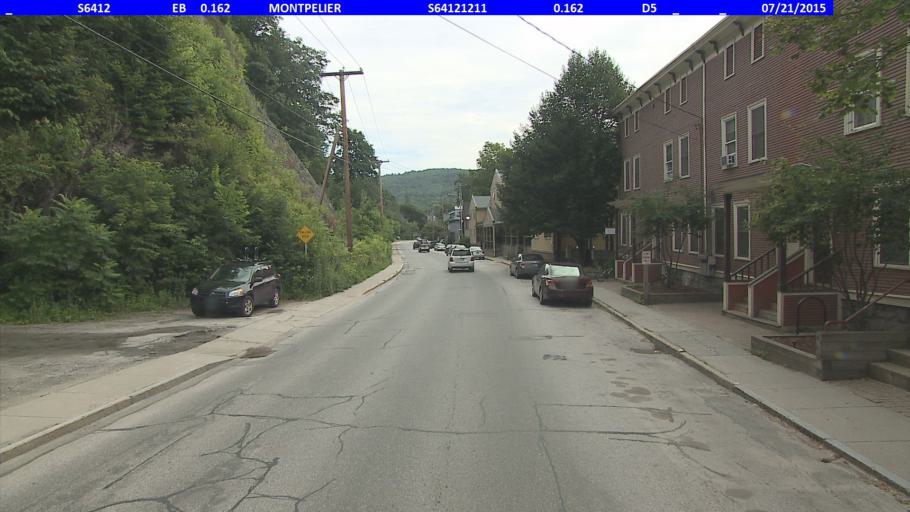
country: US
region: Vermont
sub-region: Washington County
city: Montpelier
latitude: 44.2621
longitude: -72.5748
